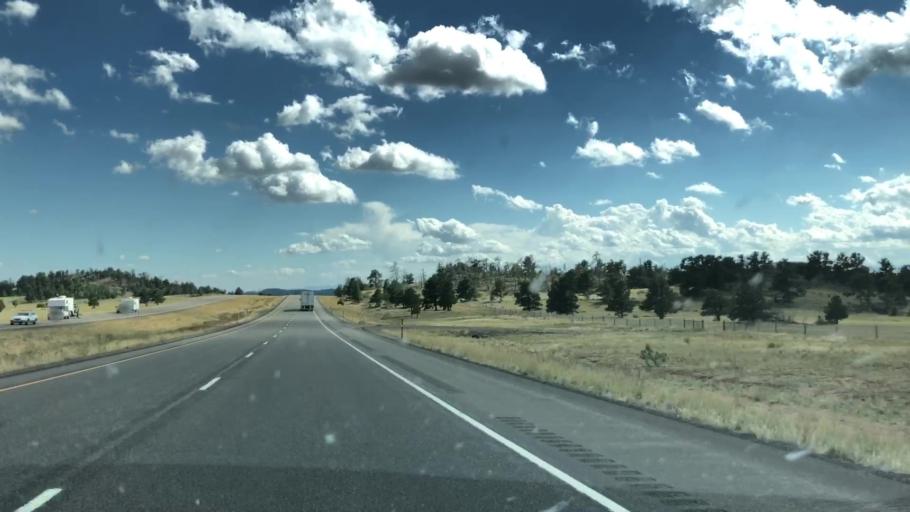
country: US
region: Wyoming
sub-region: Albany County
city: Laramie
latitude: 41.0175
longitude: -105.4209
